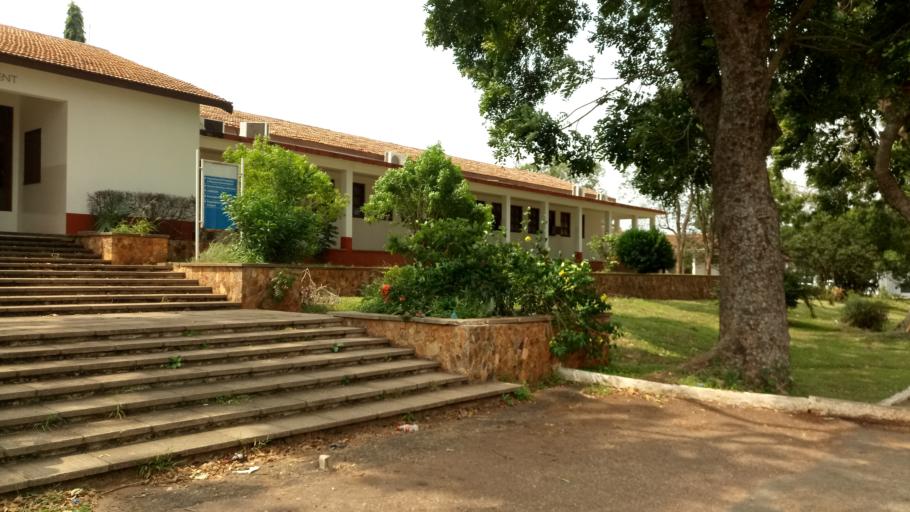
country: GH
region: Greater Accra
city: Medina Estates
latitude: 5.6506
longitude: -0.1834
